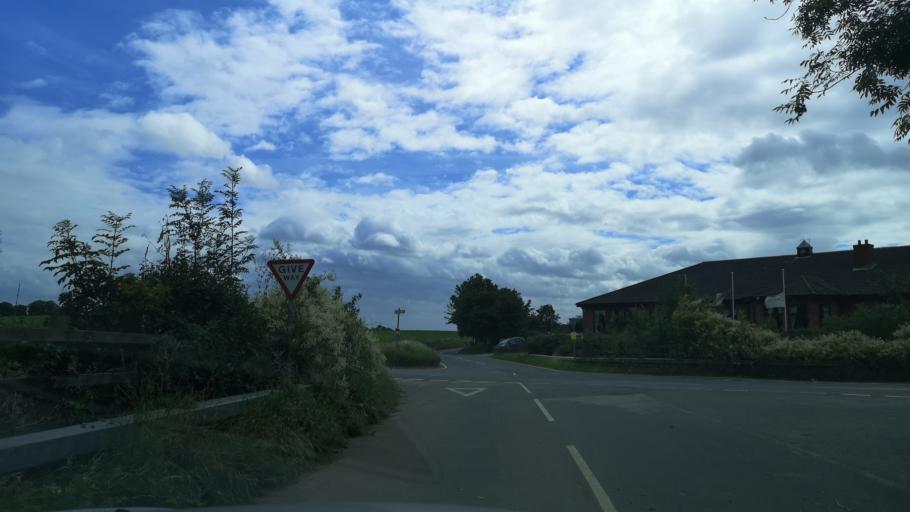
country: GB
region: England
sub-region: City and Borough of Wakefield
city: Darrington
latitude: 53.6780
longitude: -1.2575
